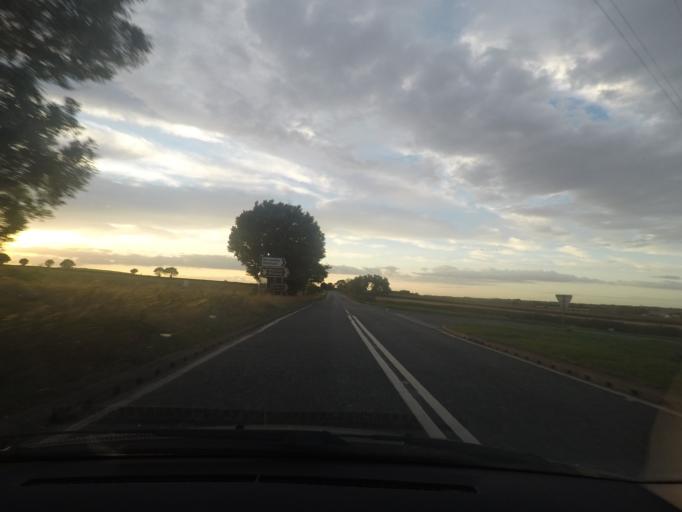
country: GB
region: England
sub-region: North East Lincolnshire
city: Laceby
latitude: 53.5071
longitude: -0.1510
